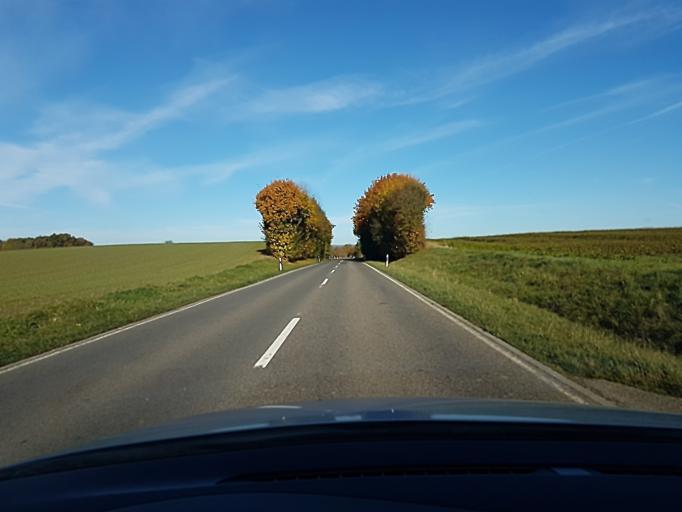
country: DE
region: Baden-Wuerttemberg
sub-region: Karlsruhe Region
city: Mosbach
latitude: 49.3665
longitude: 9.2029
